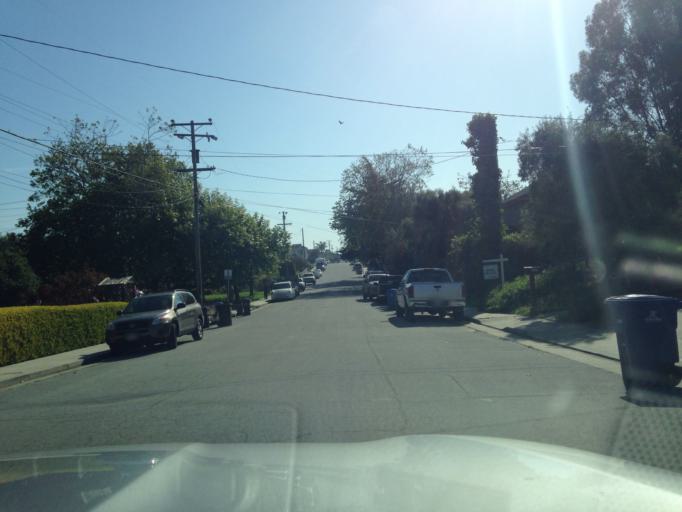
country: US
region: California
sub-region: Santa Cruz County
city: Santa Cruz
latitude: 36.9542
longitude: -122.0398
